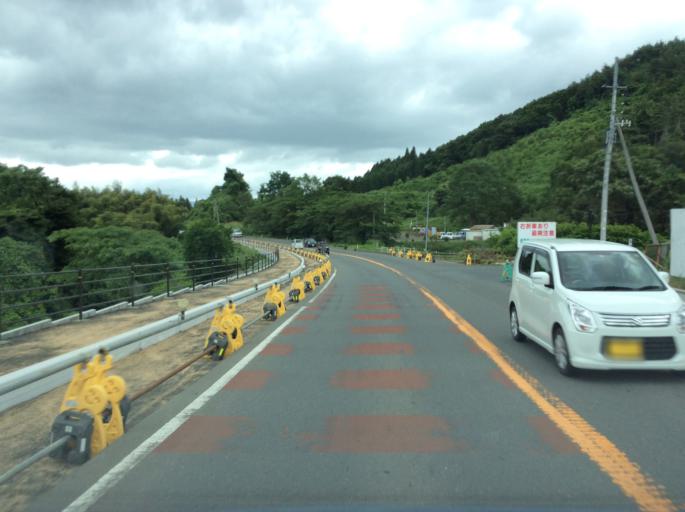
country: JP
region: Fukushima
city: Fukushima-shi
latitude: 37.7084
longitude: 140.5061
